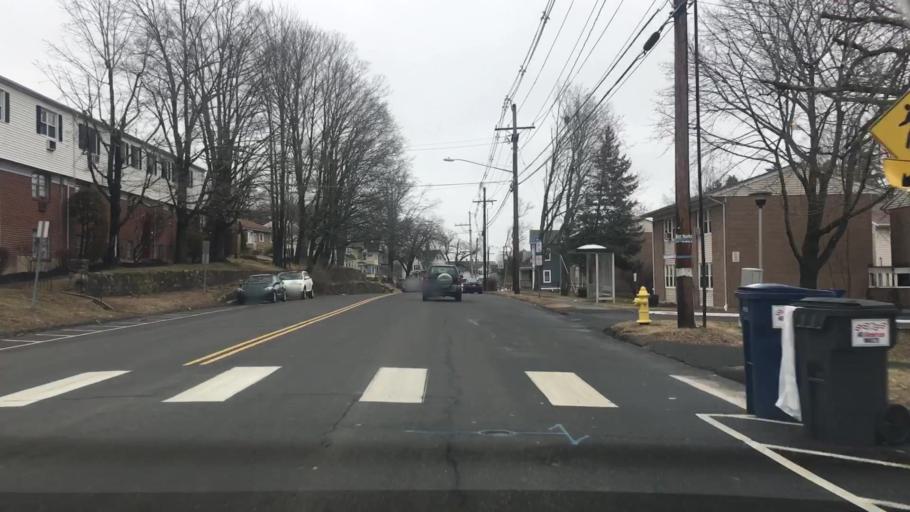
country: US
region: Connecticut
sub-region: Fairfield County
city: Danbury
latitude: 41.3843
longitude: -73.4601
